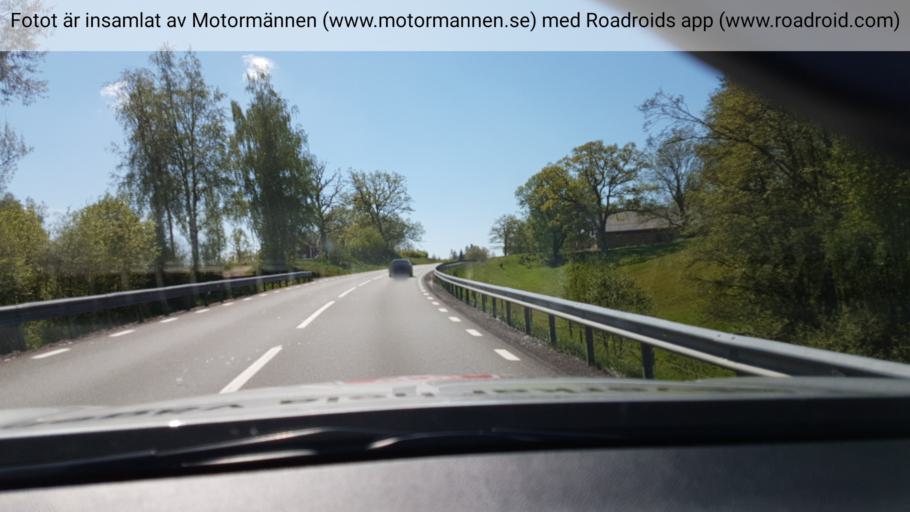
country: SE
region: Joenkoeping
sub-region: Mullsjo Kommun
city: Mullsjoe
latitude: 57.8568
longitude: 13.8583
